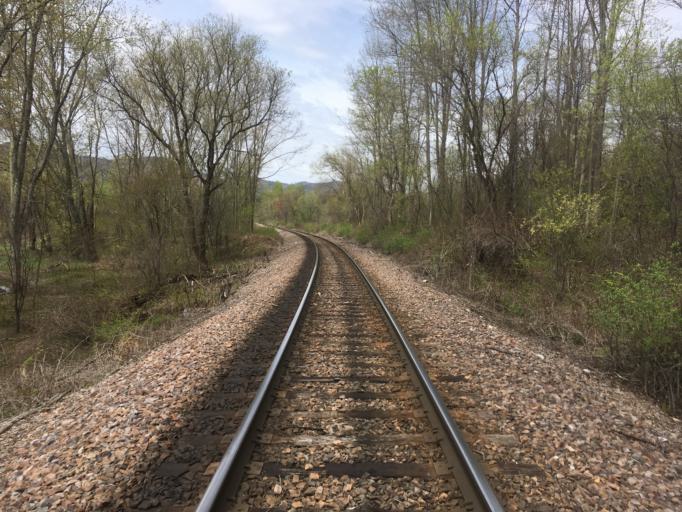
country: US
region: Vermont
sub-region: Rutland County
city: Brandon
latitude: 43.7145
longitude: -73.0431
